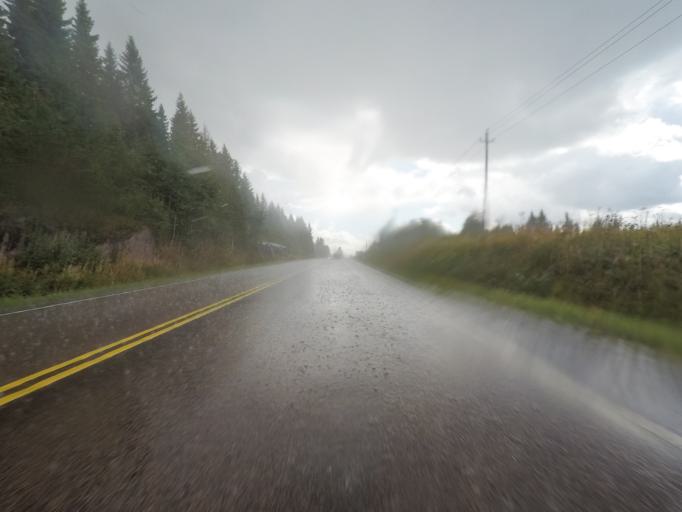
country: FI
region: Central Finland
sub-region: Joutsa
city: Leivonmaeki
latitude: 61.9226
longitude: 26.1164
